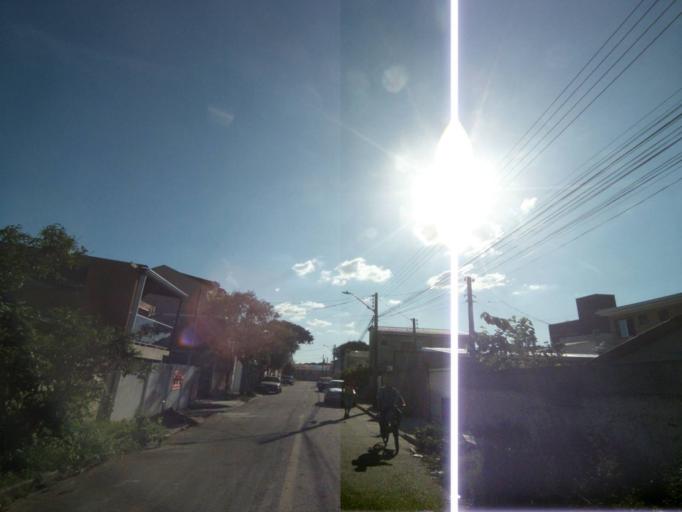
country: BR
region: Parana
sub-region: Pinhais
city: Pinhais
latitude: -25.4573
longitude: -49.2030
